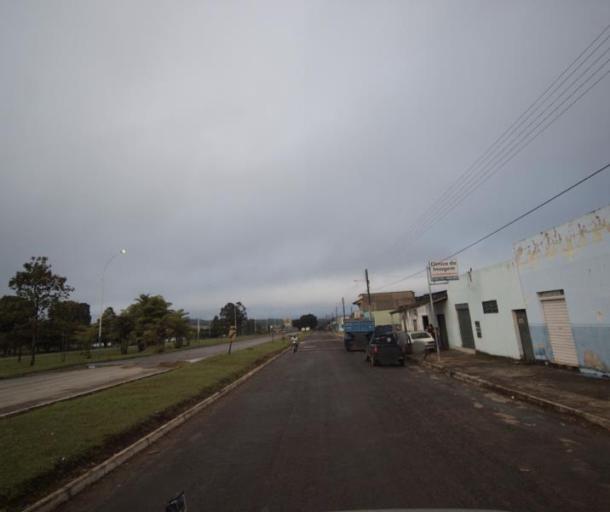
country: BR
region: Goias
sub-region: Pirenopolis
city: Pirenopolis
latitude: -15.7886
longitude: -48.7719
